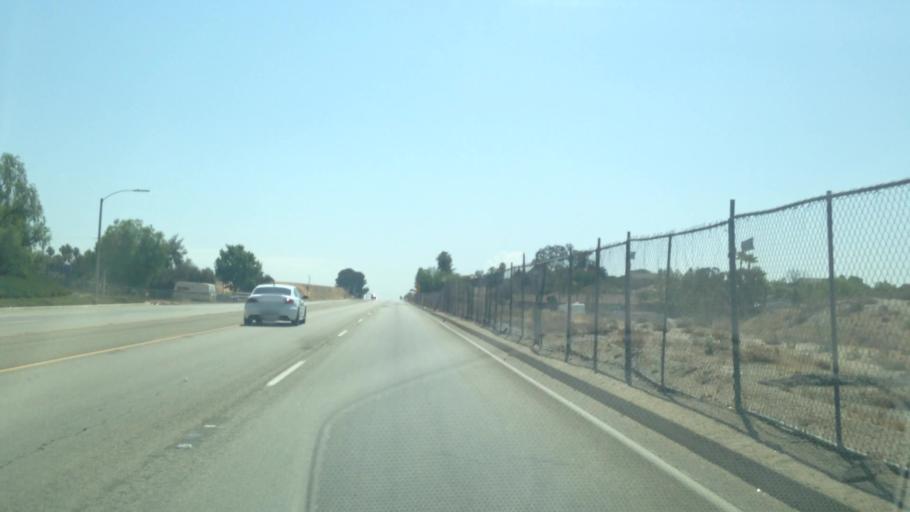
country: US
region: California
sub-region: Riverside County
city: Woodcrest
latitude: 33.8823
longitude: -117.3811
